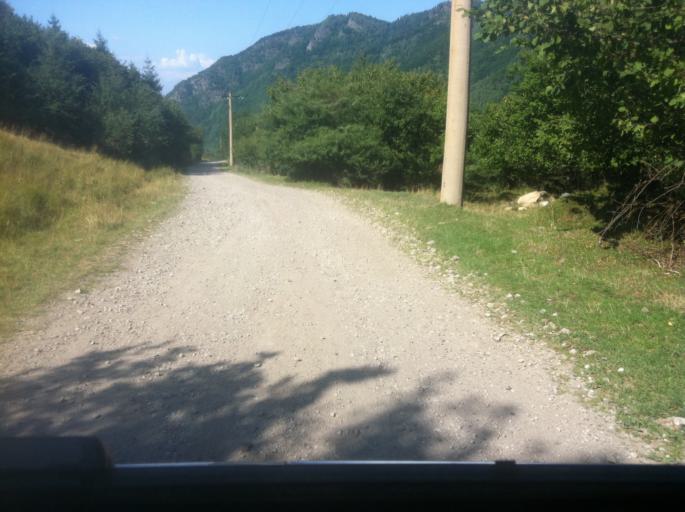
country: RO
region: Hunedoara
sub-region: Comuna Rau de Mori
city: Rau de Mori
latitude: 45.4456
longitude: 22.8941
